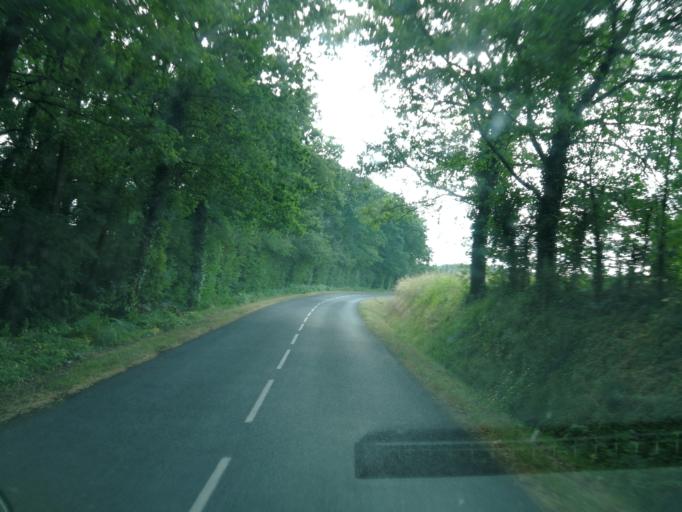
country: FR
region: Aquitaine
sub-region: Departement du Lot-et-Garonne
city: Monsempron-Libos
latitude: 44.5303
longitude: 0.9318
